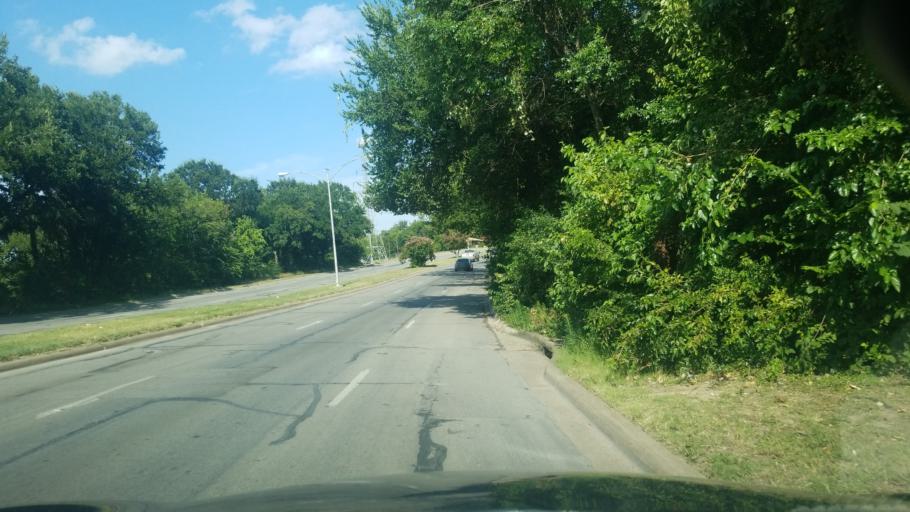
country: US
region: Texas
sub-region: Dallas County
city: Dallas
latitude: 32.7197
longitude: -96.7936
